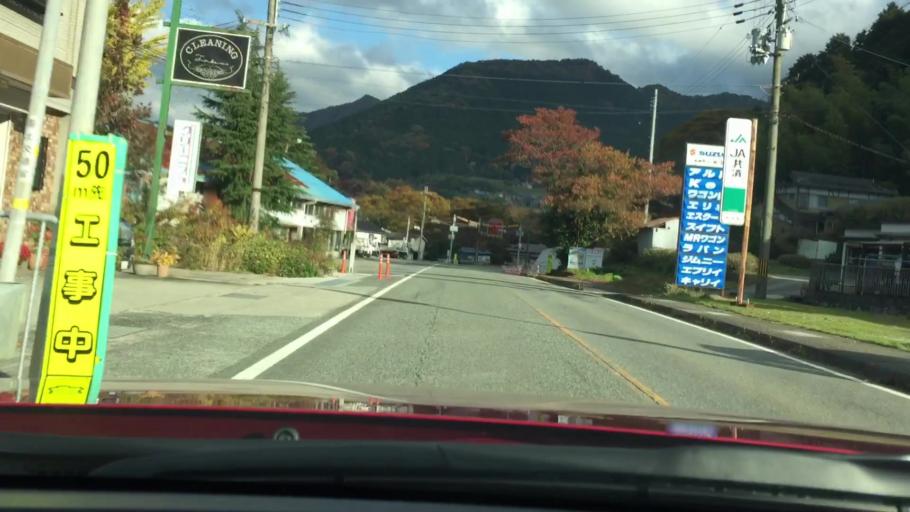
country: JP
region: Hyogo
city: Yamazakicho-nakabirose
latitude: 35.1685
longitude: 134.5441
